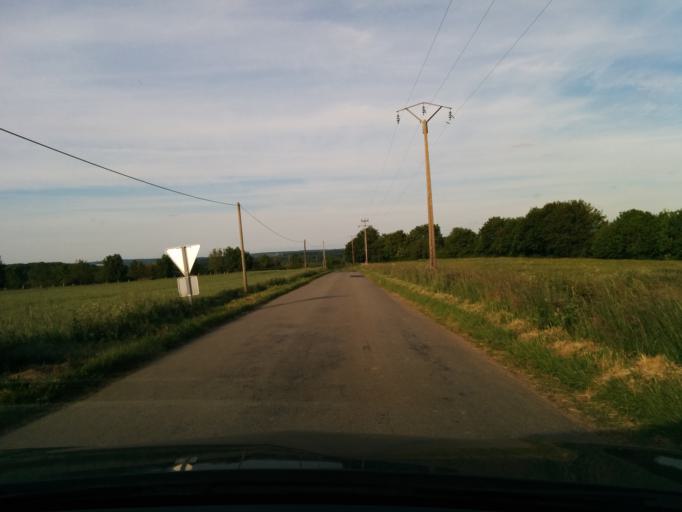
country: FR
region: Haute-Normandie
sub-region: Departement de la Seine-Maritime
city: Serqueux
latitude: 49.6374
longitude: 1.4444
